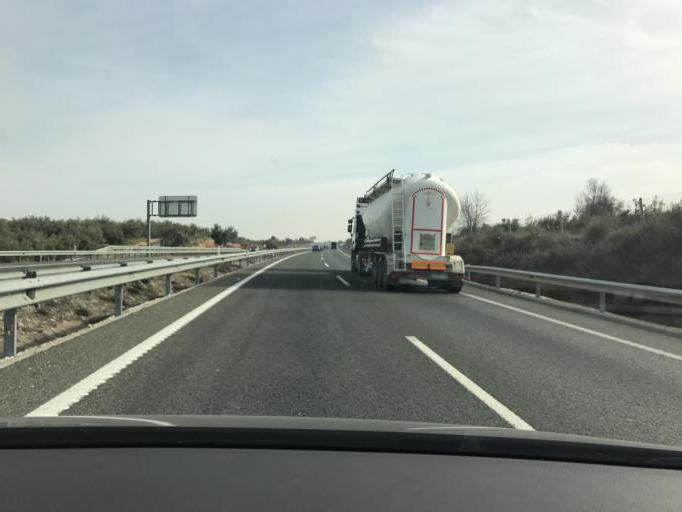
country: ES
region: Andalusia
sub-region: Provincia de Granada
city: Villanueva de Mesia
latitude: 37.1938
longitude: -3.9886
